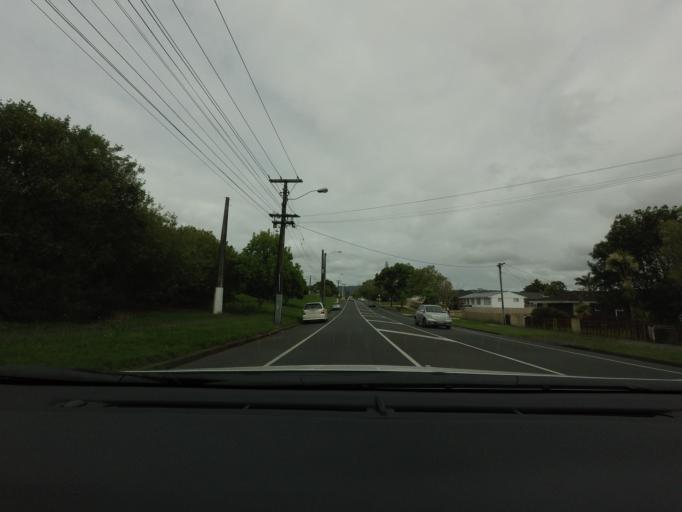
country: NZ
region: Auckland
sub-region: Auckland
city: Waitakere
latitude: -36.8920
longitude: 174.6222
